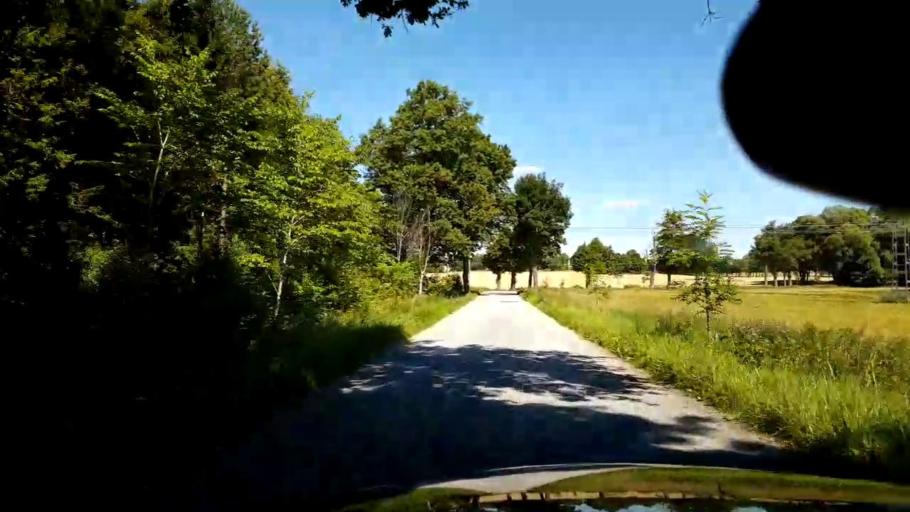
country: SE
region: Stockholm
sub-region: Upplands-Bro Kommun
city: Bro
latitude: 59.5980
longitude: 17.6423
